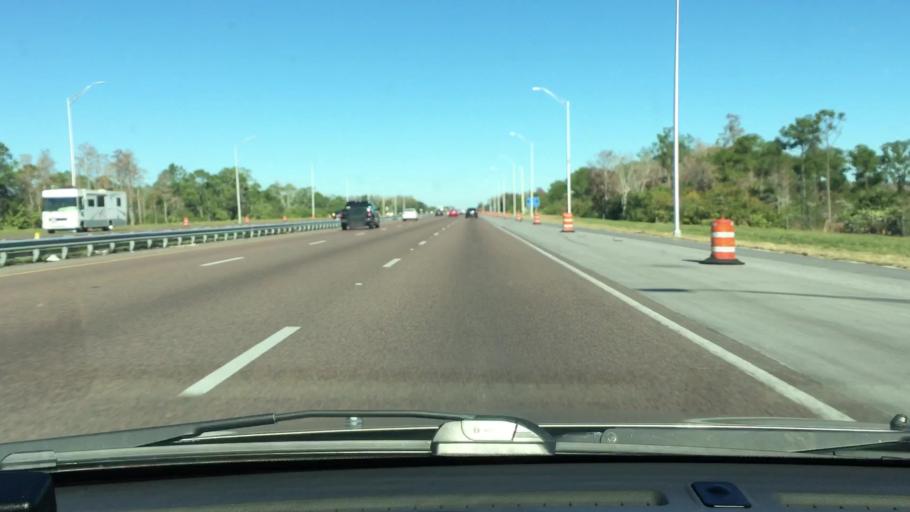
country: US
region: Florida
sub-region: Brevard County
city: Grant-Valkaria
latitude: 27.9009
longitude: -80.5960
